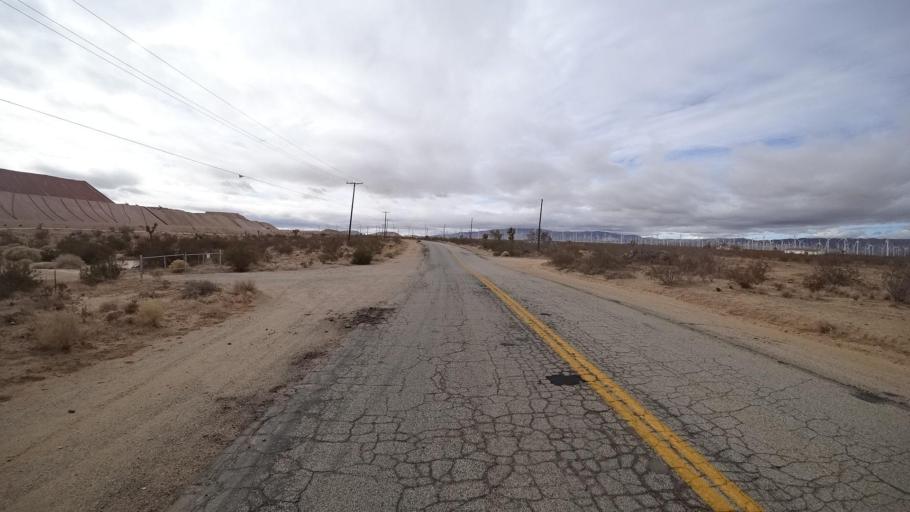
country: US
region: California
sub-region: Kern County
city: Mojave
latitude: 34.9967
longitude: -118.1952
